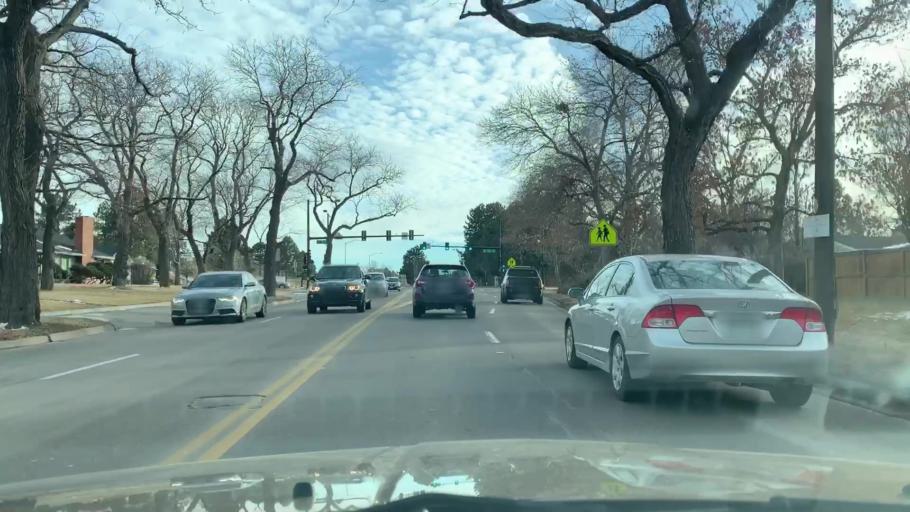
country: US
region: Colorado
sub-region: Arapahoe County
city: Glendale
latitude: 39.7192
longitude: -104.9128
